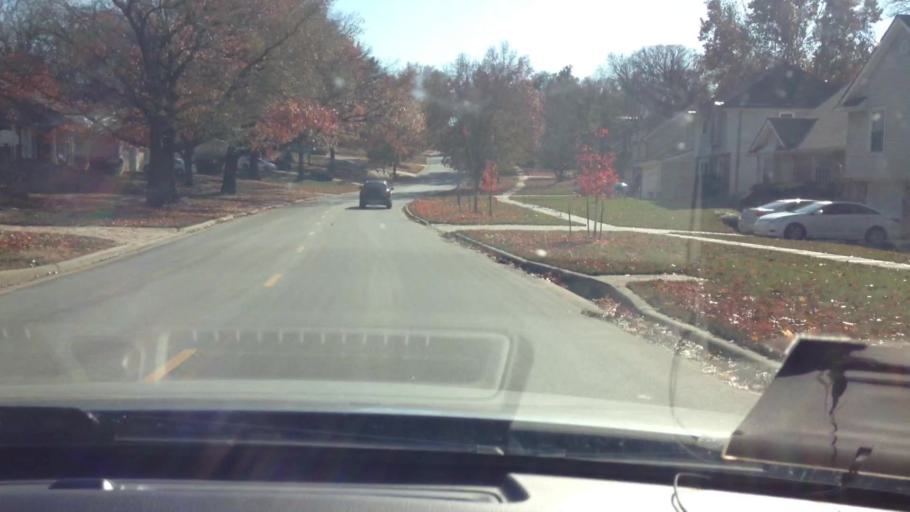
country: US
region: Kansas
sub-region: Johnson County
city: Leawood
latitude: 38.9478
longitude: -94.6391
